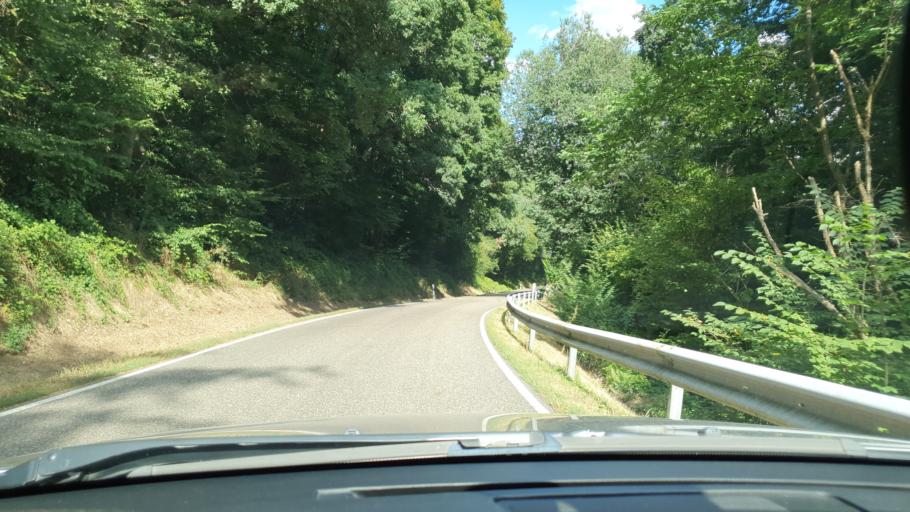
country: DE
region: Rheinland-Pfalz
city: Hoheinod
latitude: 49.2839
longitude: 7.6302
